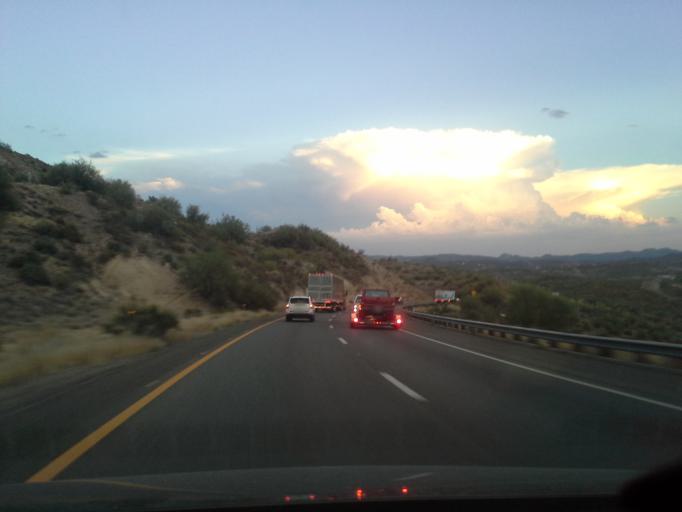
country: US
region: Arizona
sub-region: Yavapai County
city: Black Canyon City
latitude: 34.1122
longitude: -112.1444
